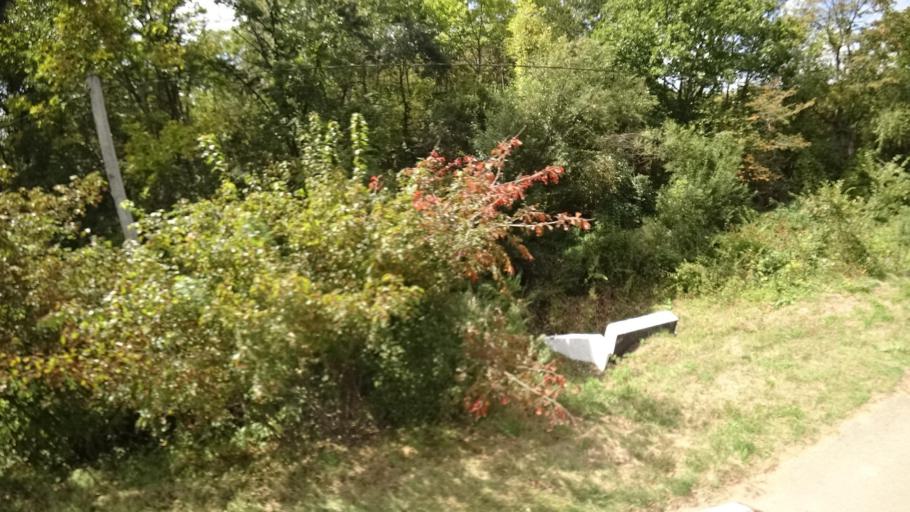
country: RU
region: Primorskiy
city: Yakovlevka
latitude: 44.7075
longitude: 133.6395
